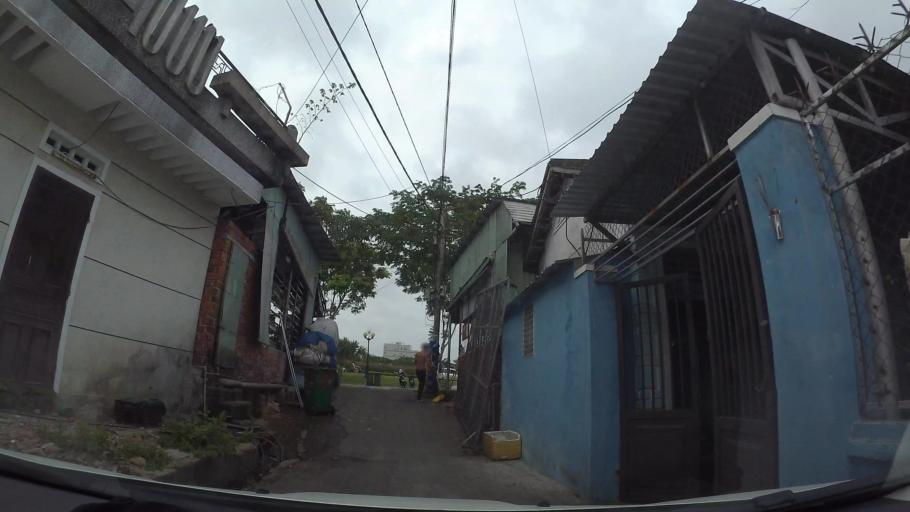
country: VN
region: Da Nang
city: Son Tra
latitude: 16.0606
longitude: 108.2316
